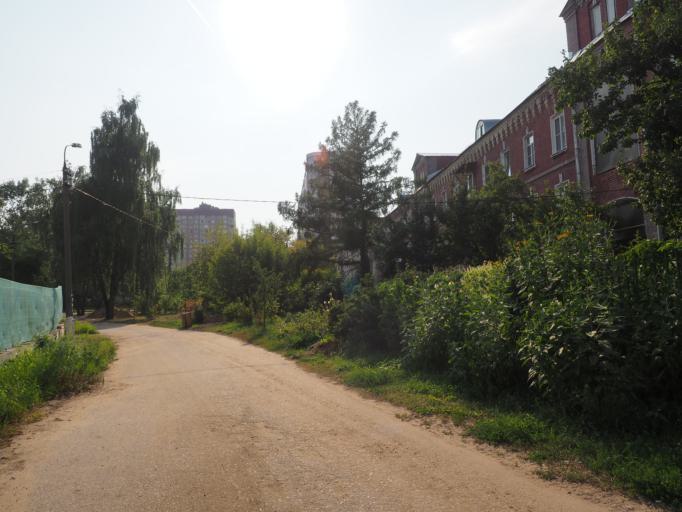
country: RU
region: Moskovskaya
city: Oktyabr'skiy
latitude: 55.6075
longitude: 37.9739
